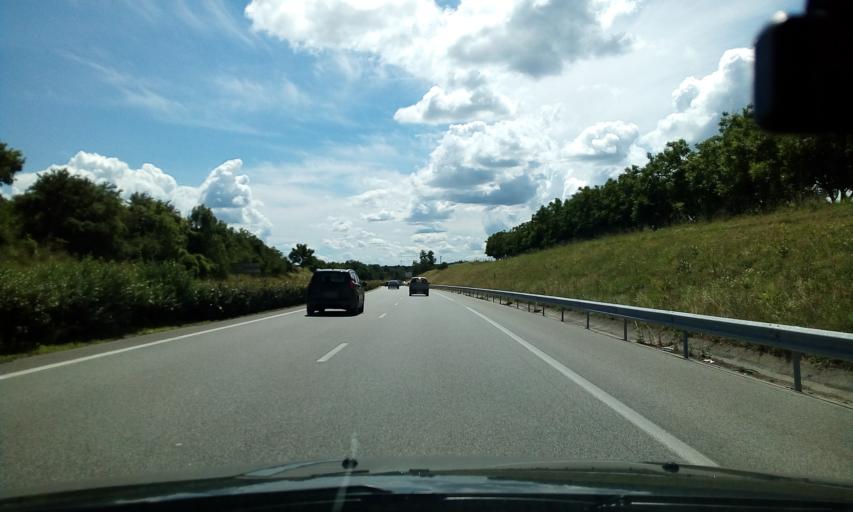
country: FR
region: Rhone-Alpes
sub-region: Departement de l'Isere
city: Saint-Sauveur
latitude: 45.1446
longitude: 5.3425
